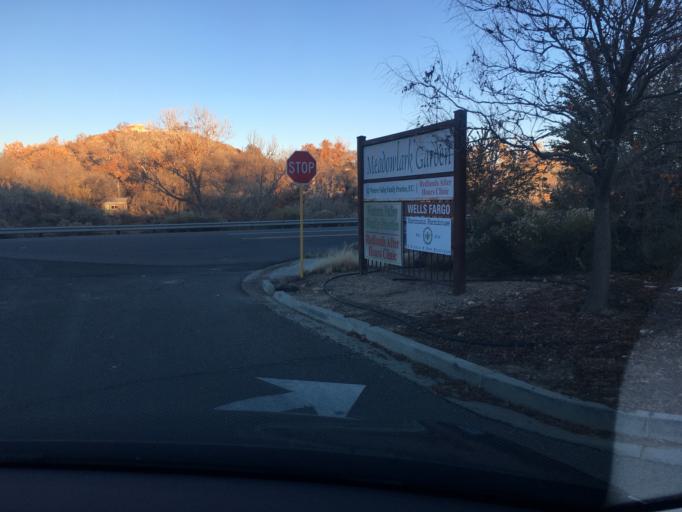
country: US
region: Colorado
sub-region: Mesa County
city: Redlands
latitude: 39.0766
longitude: -108.6359
